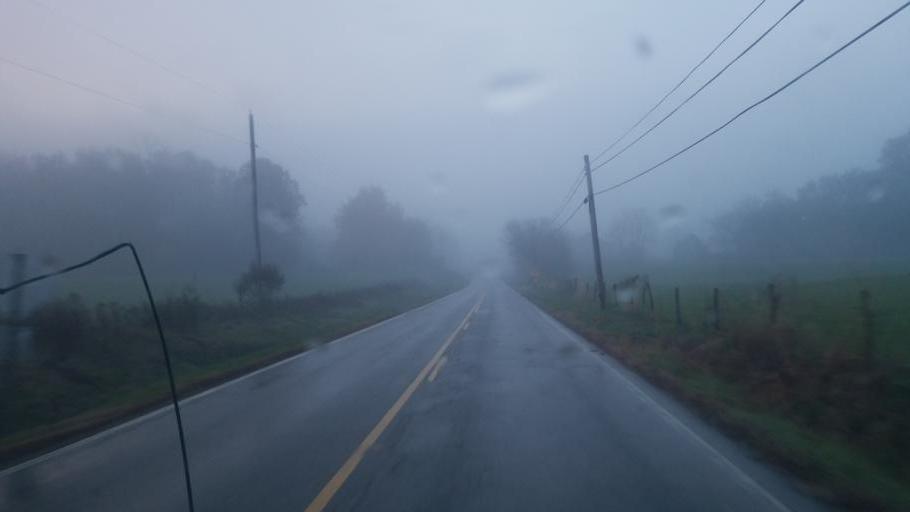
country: US
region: Ohio
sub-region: Morgan County
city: McConnelsville
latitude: 39.5051
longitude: -81.8562
